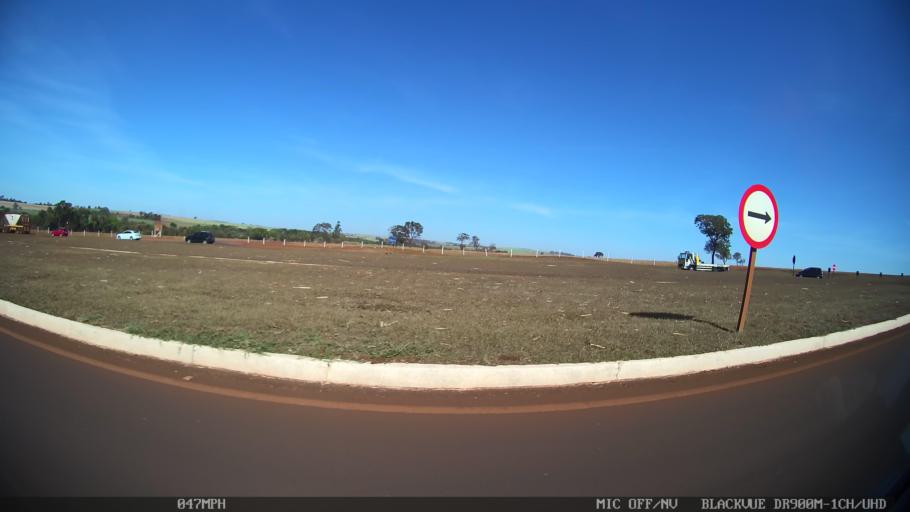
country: BR
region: Sao Paulo
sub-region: Sao Joaquim Da Barra
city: Sao Joaquim da Barra
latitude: -20.5129
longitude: -47.8980
